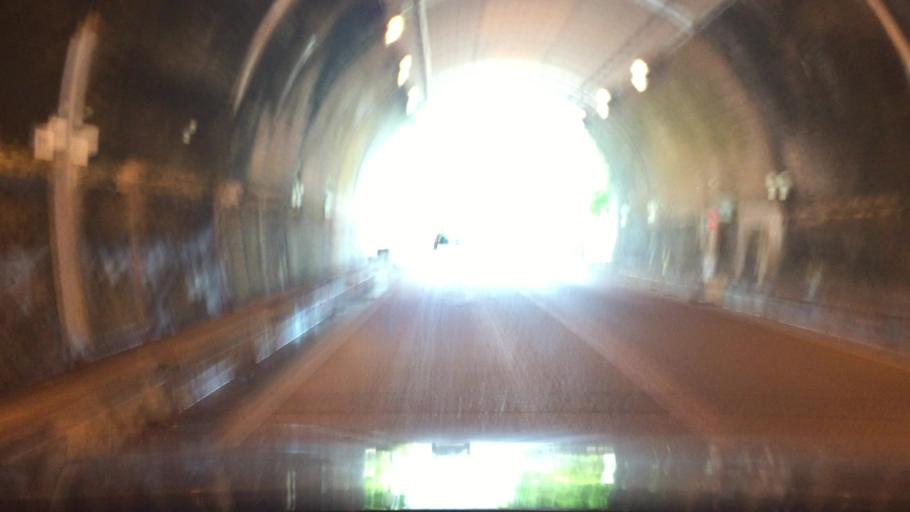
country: JP
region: Okinawa
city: Ishigaki
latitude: 24.4477
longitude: 124.2109
